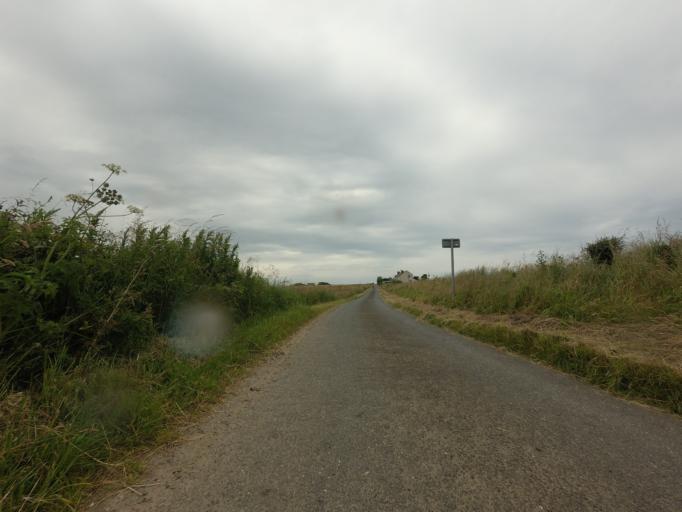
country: GB
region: Scotland
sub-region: Aberdeenshire
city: Portsoy
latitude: 57.6770
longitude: -2.6670
